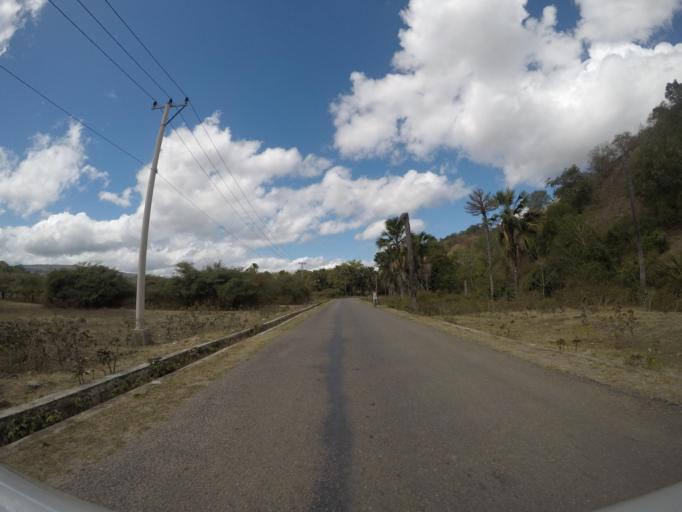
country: TL
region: Lautem
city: Lospalos
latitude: -8.4124
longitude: 126.8271
